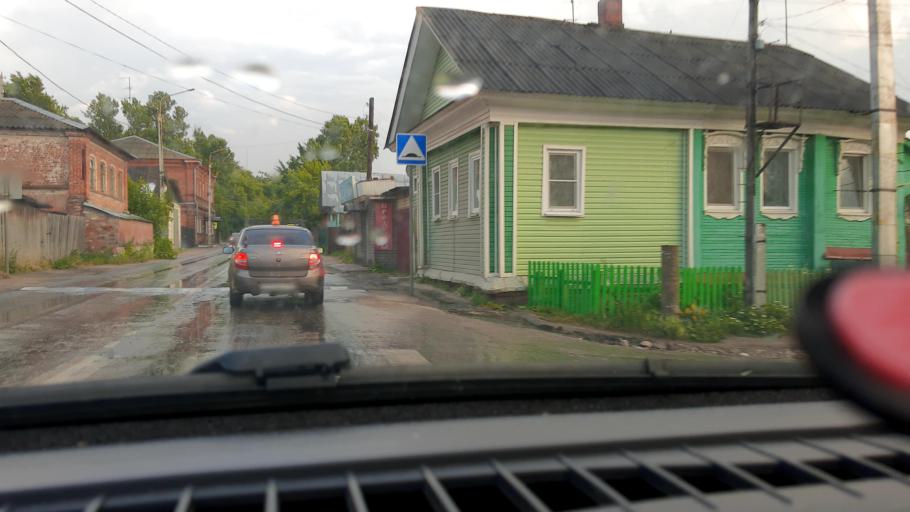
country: RU
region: Nizjnij Novgorod
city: Gorodets
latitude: 56.6512
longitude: 43.4650
